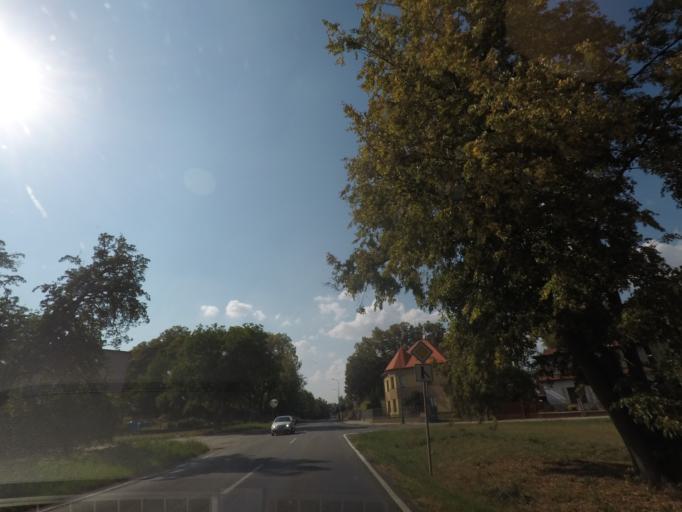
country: CZ
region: Kralovehradecky
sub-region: Okres Nachod
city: Jaromer
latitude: 50.3351
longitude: 15.9360
